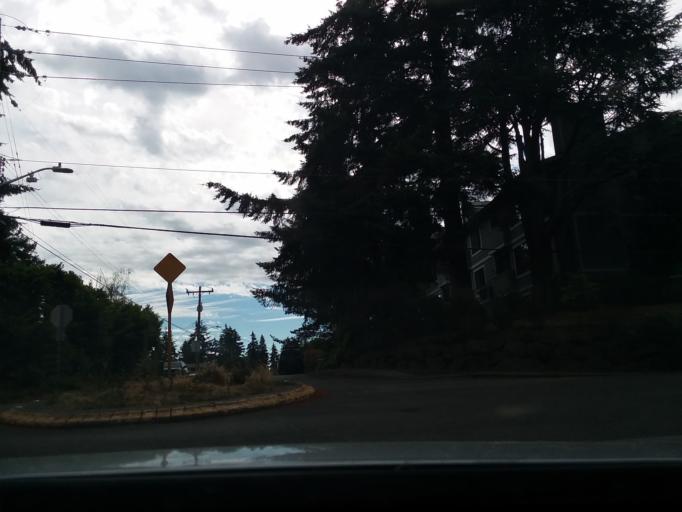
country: US
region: Washington
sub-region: King County
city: Shoreline
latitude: 47.7469
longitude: -122.3482
